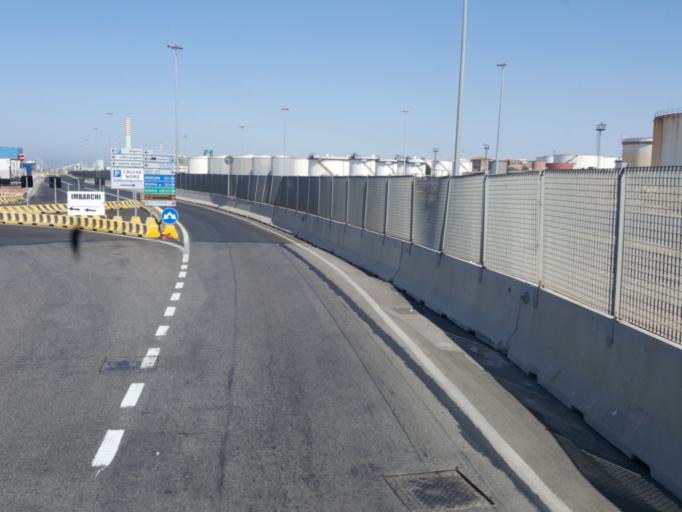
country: IT
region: Latium
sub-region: Citta metropolitana di Roma Capitale
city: Civitavecchia
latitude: 42.1034
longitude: 11.7817
